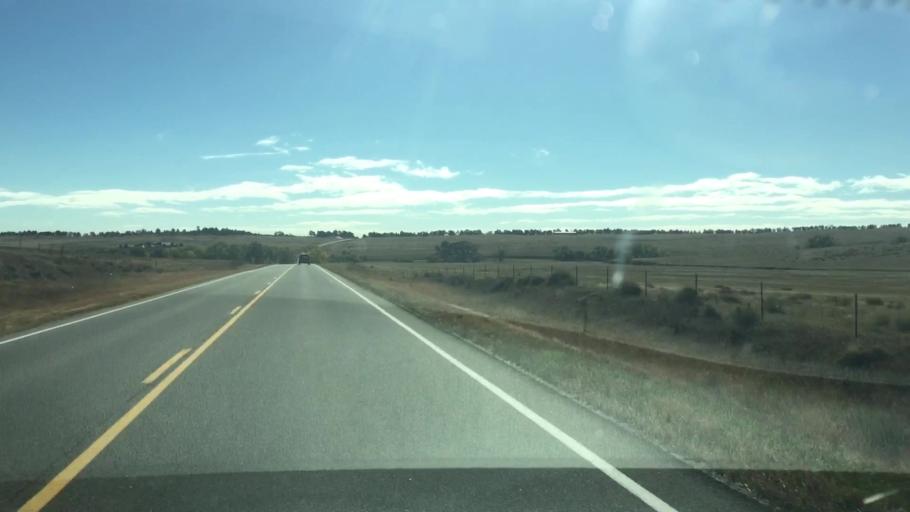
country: US
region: Colorado
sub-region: Elbert County
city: Kiowa
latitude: 39.3238
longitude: -104.3905
